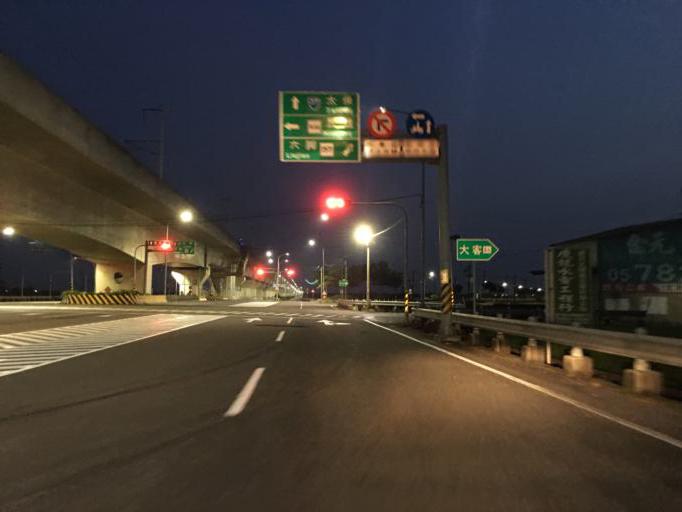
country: TW
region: Taiwan
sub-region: Chiayi
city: Taibao
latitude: 23.5327
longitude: 120.3272
